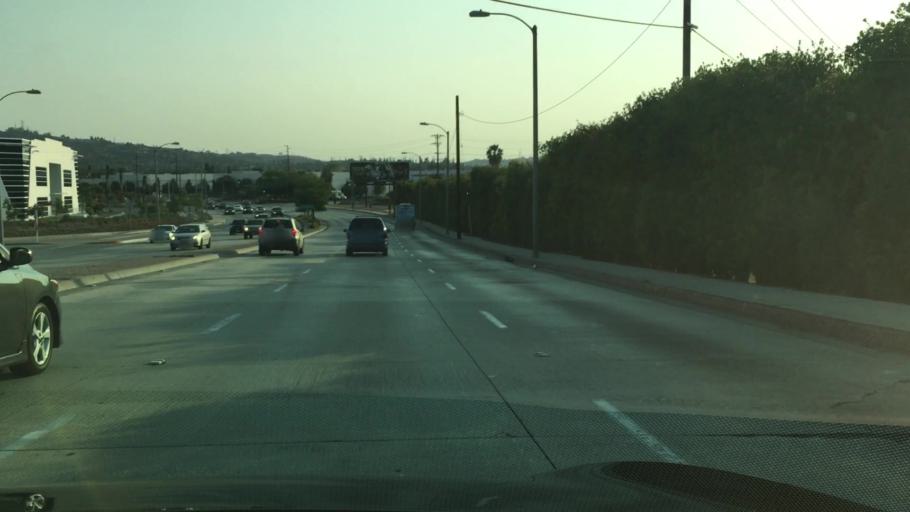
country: US
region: California
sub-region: Los Angeles County
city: South San Jose Hills
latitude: 34.0078
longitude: -117.9274
